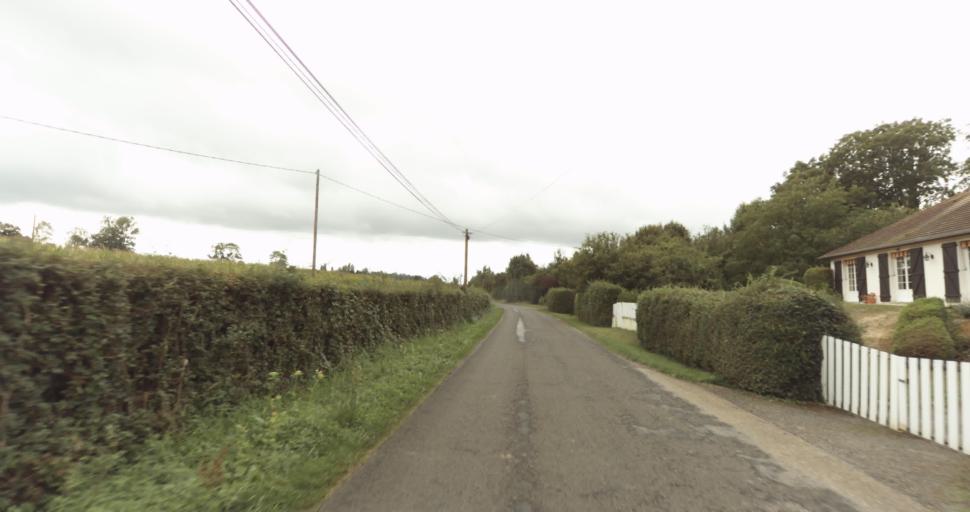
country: FR
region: Lower Normandy
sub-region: Departement de l'Orne
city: Vimoutiers
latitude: 48.8953
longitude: 0.1822
